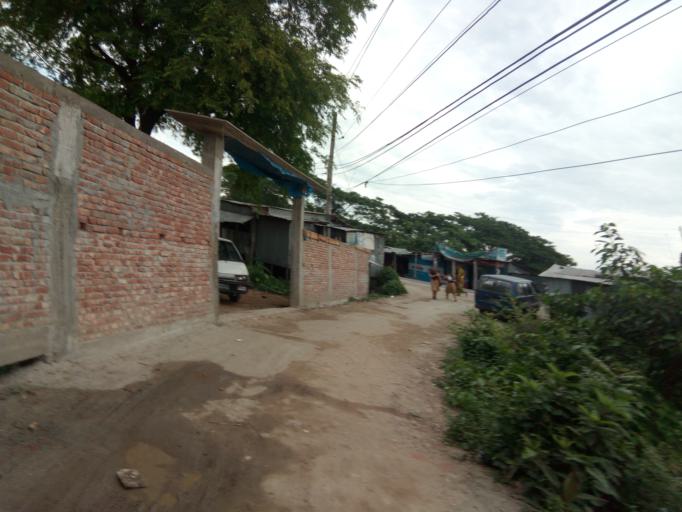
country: BD
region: Dhaka
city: Paltan
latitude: 23.7397
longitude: 90.4798
